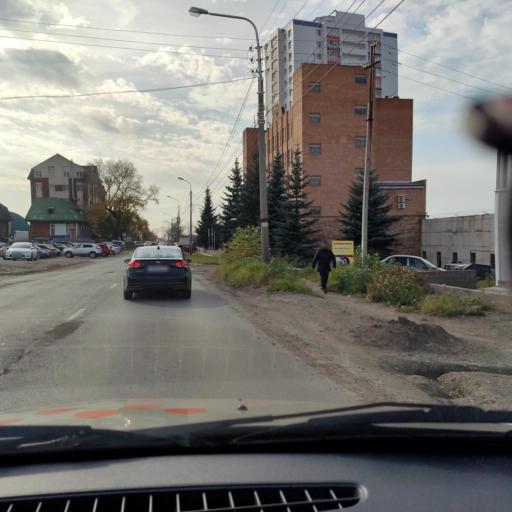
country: RU
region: Bashkortostan
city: Ufa
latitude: 54.7077
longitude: 55.9768
